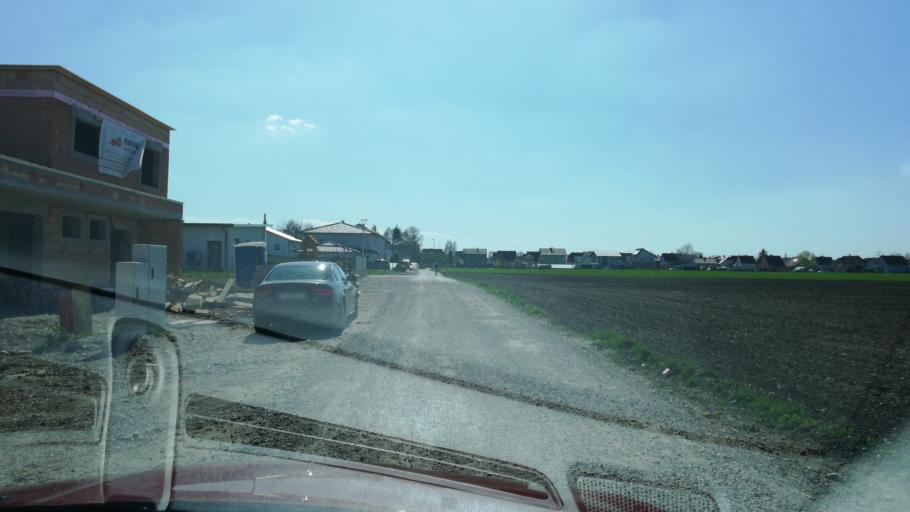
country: AT
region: Upper Austria
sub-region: Politischer Bezirk Linz-Land
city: Horsching
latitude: 48.2094
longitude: 14.1954
